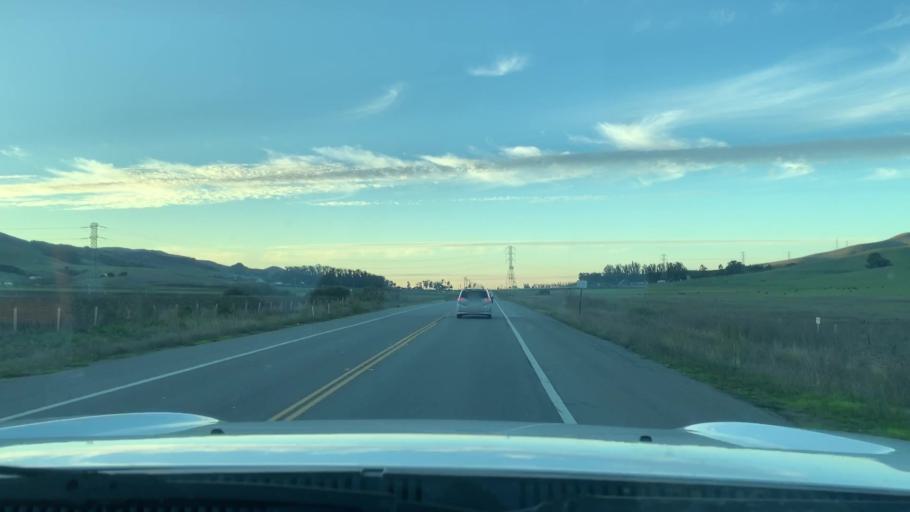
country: US
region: California
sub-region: San Luis Obispo County
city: San Luis Obispo
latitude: 35.2798
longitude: -120.7198
